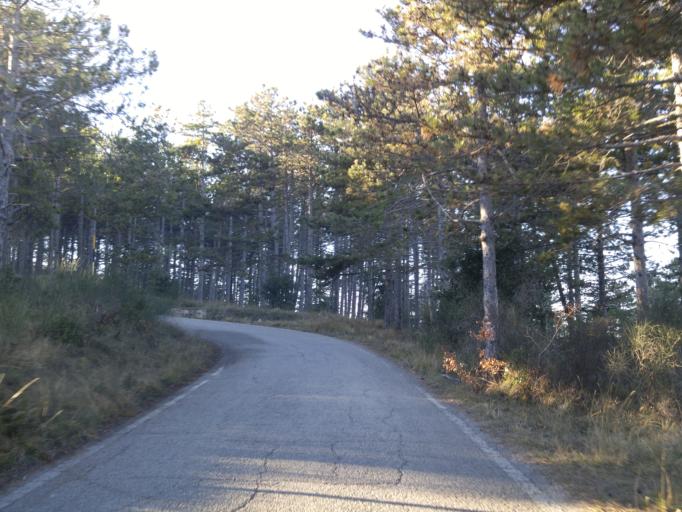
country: IT
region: The Marches
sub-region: Provincia di Pesaro e Urbino
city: Isola del Piano
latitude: 43.7028
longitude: 12.7735
